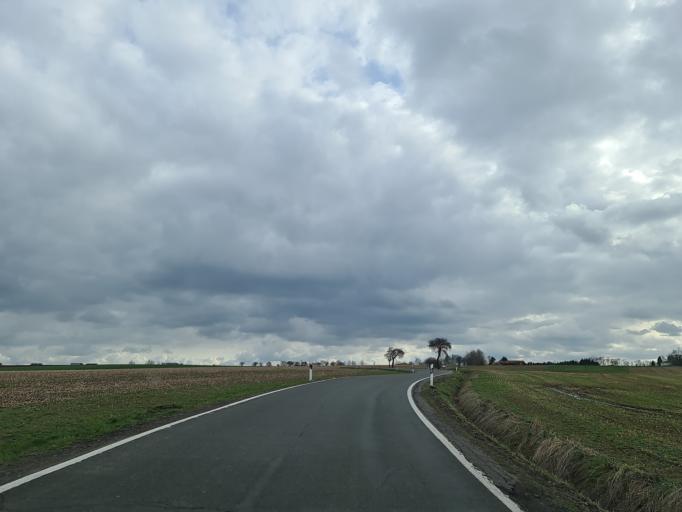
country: DE
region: Saxony
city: Wildenfels
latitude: 50.6939
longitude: 12.6114
